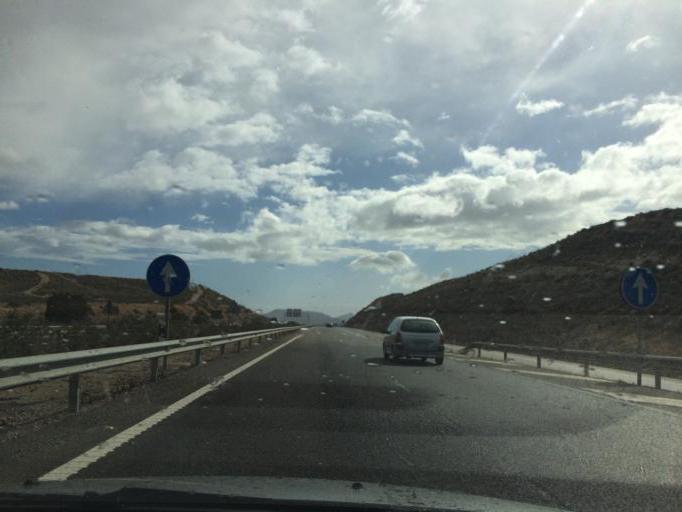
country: ES
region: Andalusia
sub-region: Provincia de Almeria
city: Retamar
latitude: 36.8641
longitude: -2.2666
